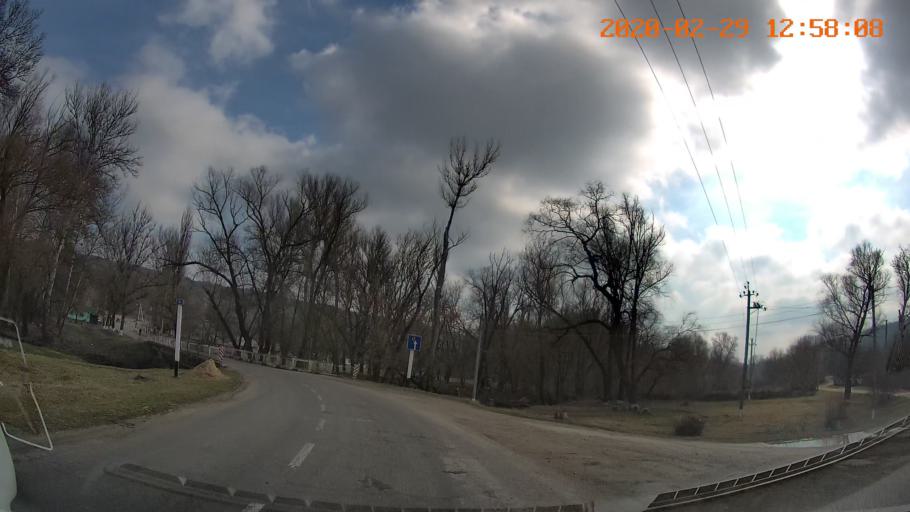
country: MD
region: Telenesti
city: Camenca
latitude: 48.0711
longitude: 28.7179
